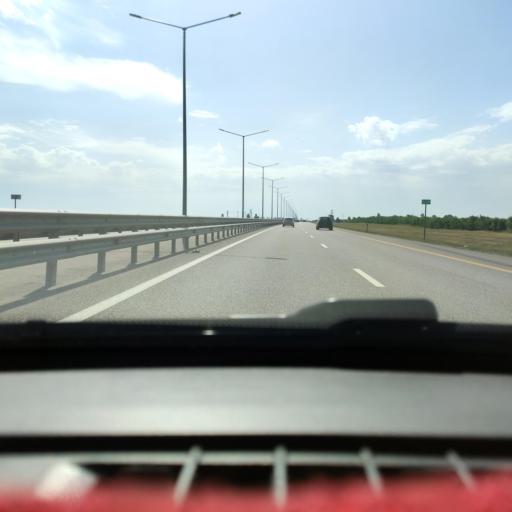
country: RU
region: Voronezj
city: Novaya Usman'
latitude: 51.6001
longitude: 39.3456
